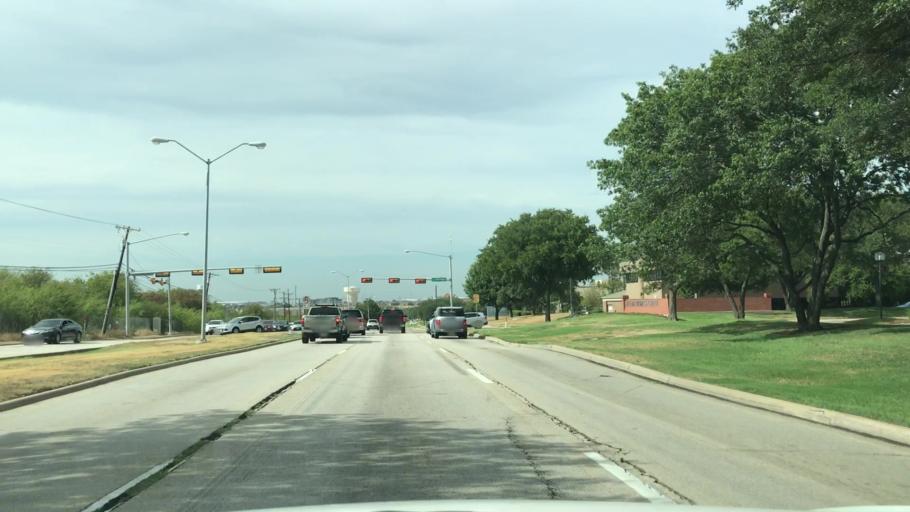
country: US
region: Texas
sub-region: Dallas County
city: Coppell
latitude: 32.8932
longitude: -96.9910
